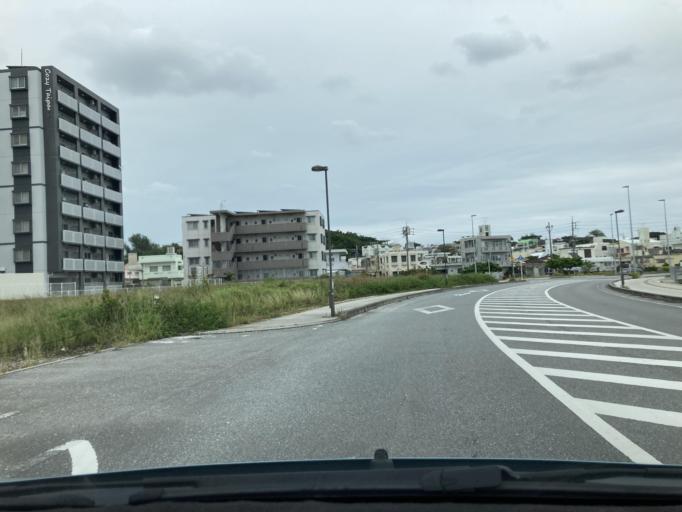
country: JP
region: Okinawa
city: Itoman
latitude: 26.1341
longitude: 127.6680
